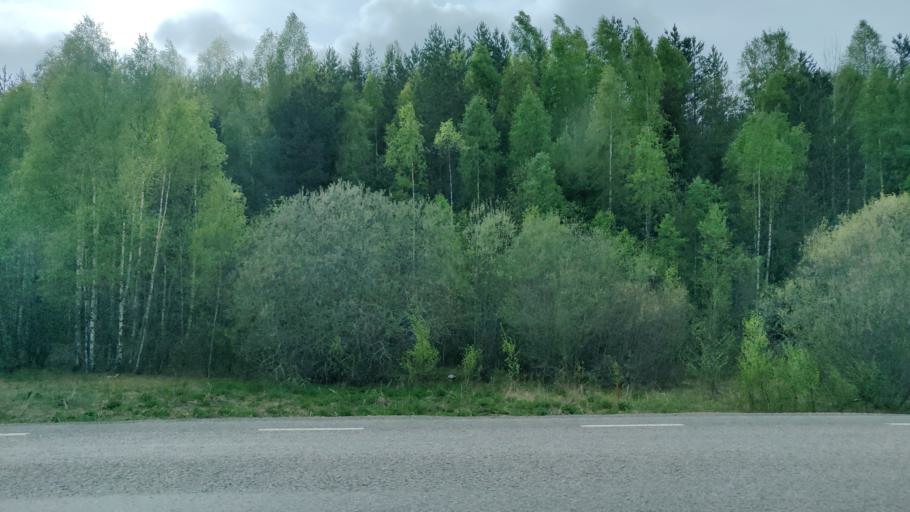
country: SE
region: Vaermland
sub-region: Forshaga Kommun
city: Deje
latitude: 59.6144
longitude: 13.4493
